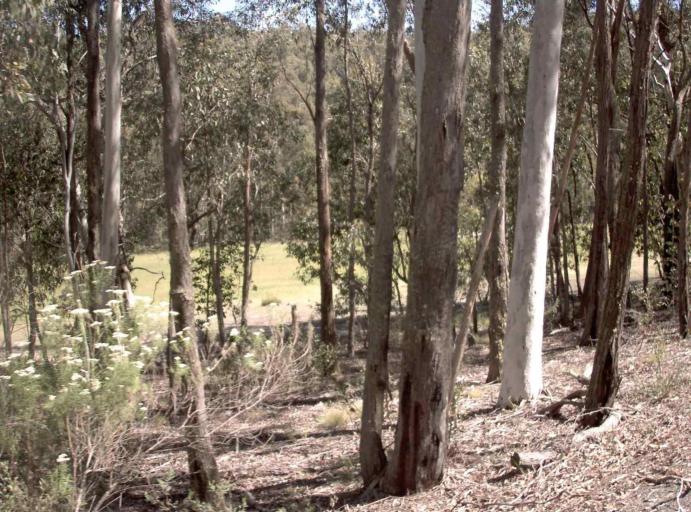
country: AU
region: New South Wales
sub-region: Bombala
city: Bombala
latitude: -37.1410
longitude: 148.7290
